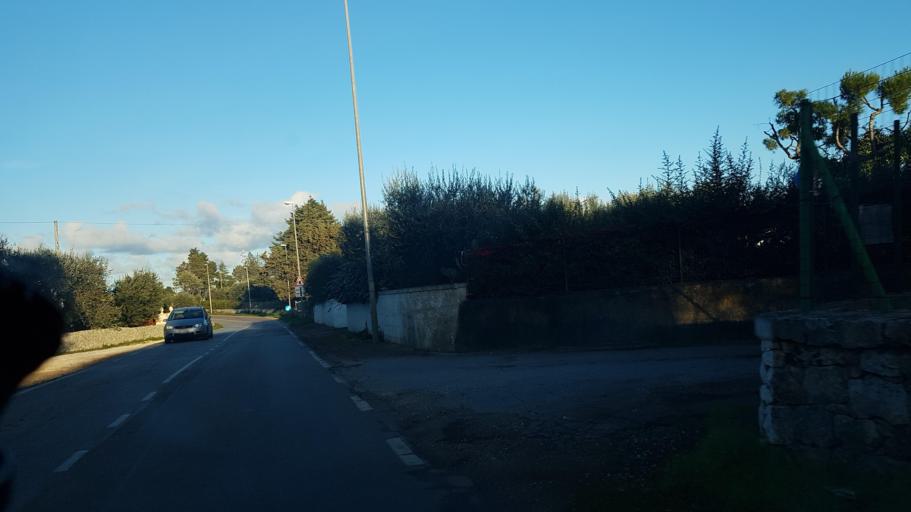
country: IT
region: Apulia
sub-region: Provincia di Brindisi
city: Ostuni
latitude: 40.7097
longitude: 17.5445
